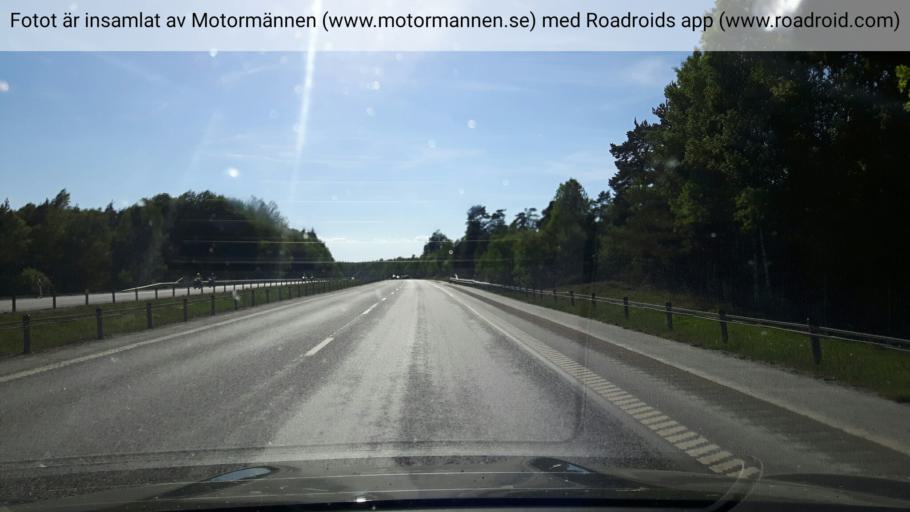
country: SE
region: Stockholm
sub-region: Norrtalje Kommun
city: Norrtalje
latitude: 59.7438
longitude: 18.6326
